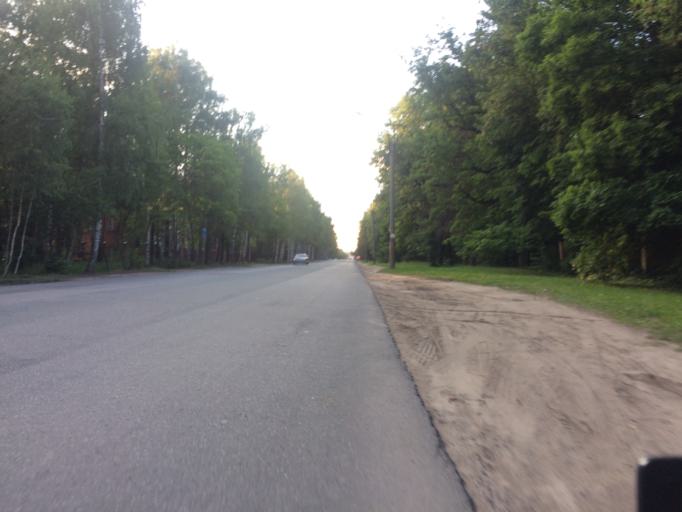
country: RU
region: Mariy-El
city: Yoshkar-Ola
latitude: 56.6219
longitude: 47.9554
